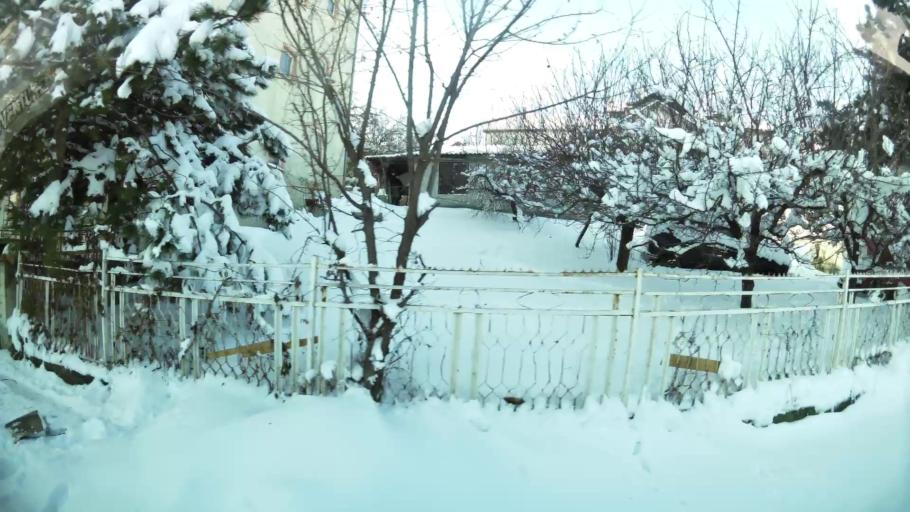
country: RS
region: Central Serbia
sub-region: Belgrade
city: Palilula
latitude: 44.7930
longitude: 20.5225
